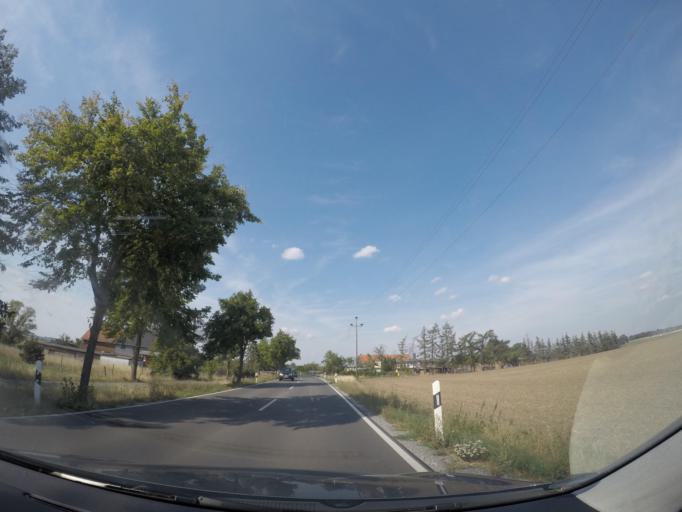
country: DE
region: Saxony-Anhalt
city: Langeln
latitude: 51.8852
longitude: 10.7698
